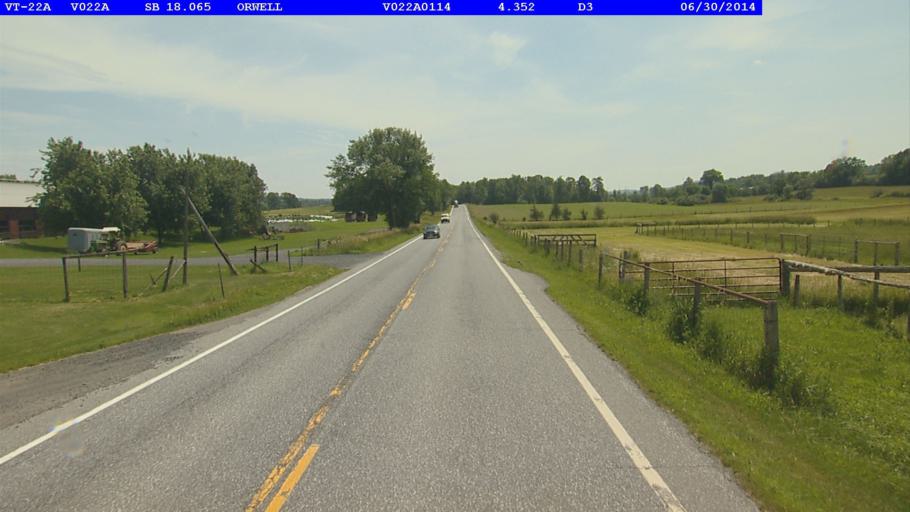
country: US
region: New York
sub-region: Essex County
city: Ticonderoga
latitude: 43.8196
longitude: -73.3064
